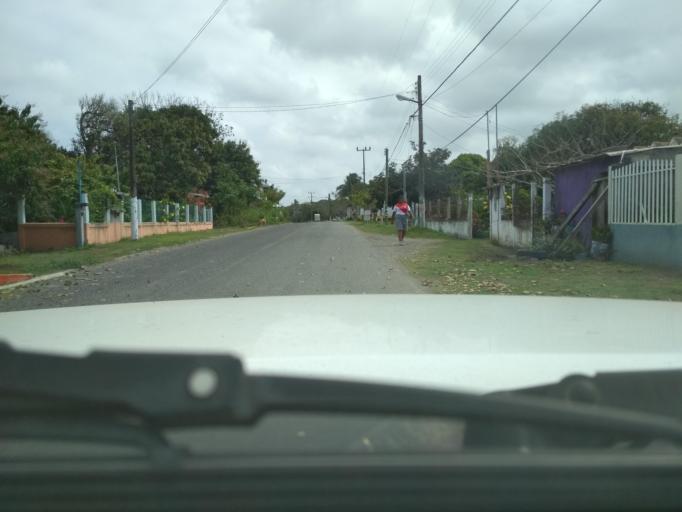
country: MX
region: Veracruz
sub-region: Veracruz
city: Delfino Victoria (Santa Fe)
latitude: 19.2526
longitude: -96.2629
